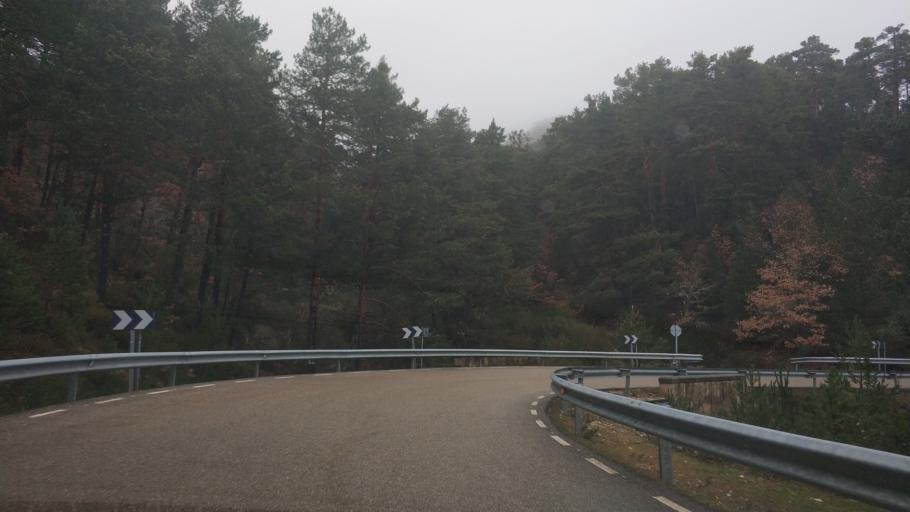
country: ES
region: Castille and Leon
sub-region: Provincia de Burgos
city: Quintanar de la Sierra
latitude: 42.0183
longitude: -3.0174
